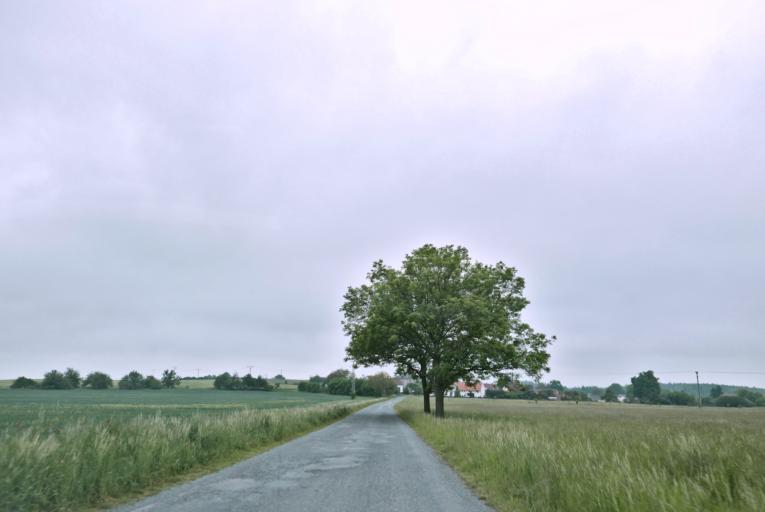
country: CZ
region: Plzensky
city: Zihle
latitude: 50.0290
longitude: 13.3249
